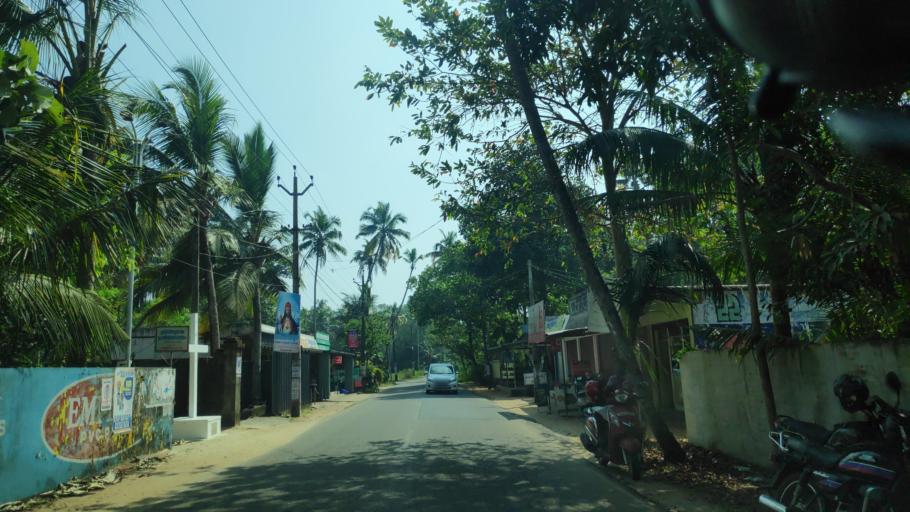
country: IN
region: Kerala
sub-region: Alappuzha
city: Vayalar
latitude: 9.6453
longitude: 76.2987
